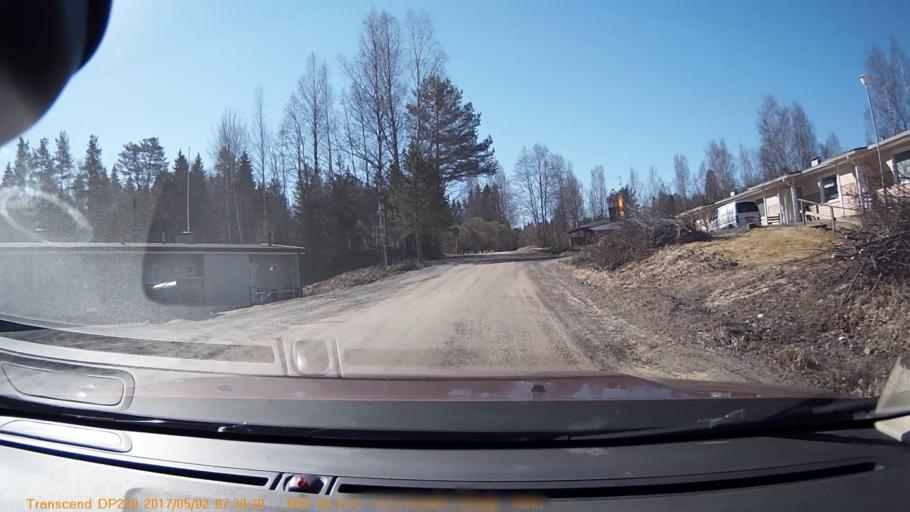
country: FI
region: Pirkanmaa
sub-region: Tampere
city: Kuru
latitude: 61.8719
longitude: 23.7280
